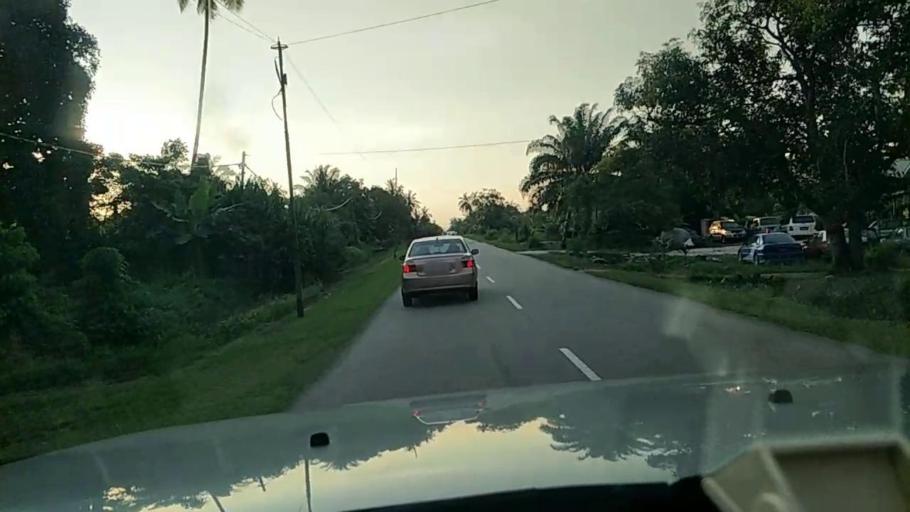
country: MY
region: Selangor
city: Kuala Selangor
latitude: 3.3101
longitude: 101.2891
